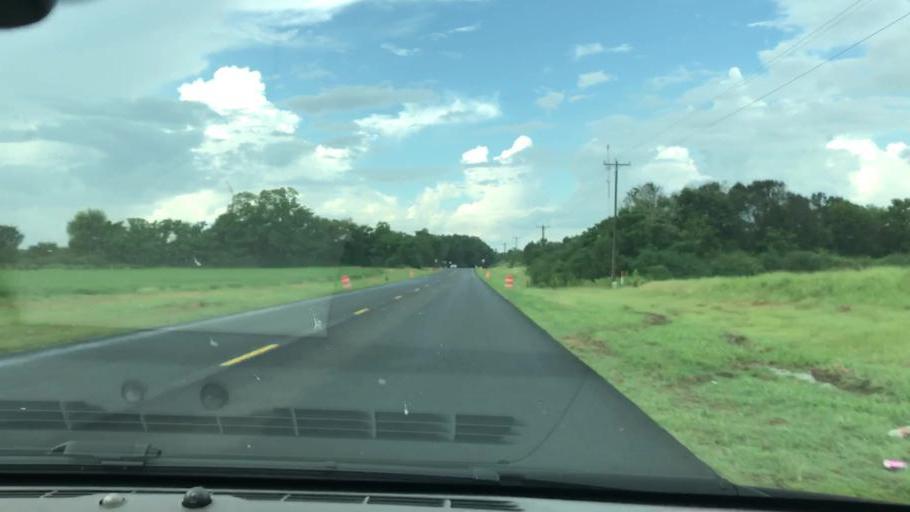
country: US
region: Georgia
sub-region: Early County
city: Blakely
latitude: 31.3978
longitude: -84.9542
